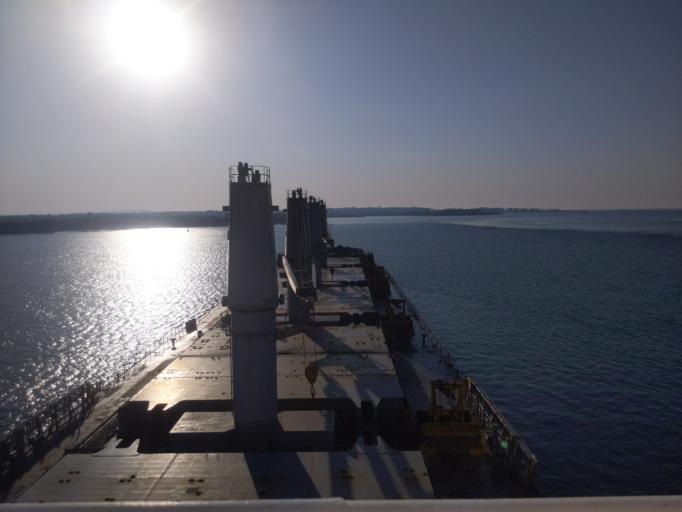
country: ZA
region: KwaZulu-Natal
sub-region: uThungulu District Municipality
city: Richards Bay
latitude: -28.8014
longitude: 32.0563
